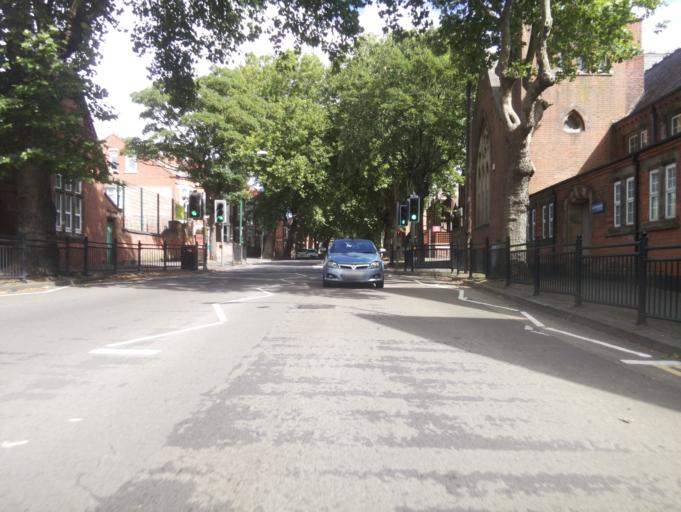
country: GB
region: England
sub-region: Nottingham
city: Nottingham
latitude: 52.9471
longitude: -1.1737
